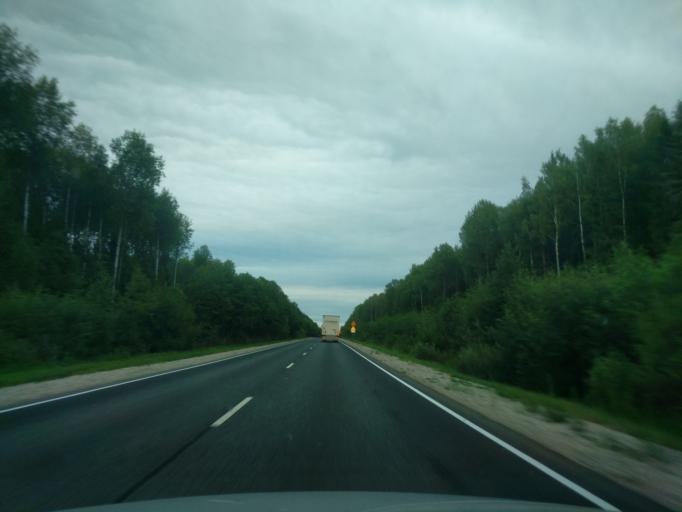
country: RU
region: Kostroma
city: Ponazyrevo
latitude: 58.3233
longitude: 46.5285
